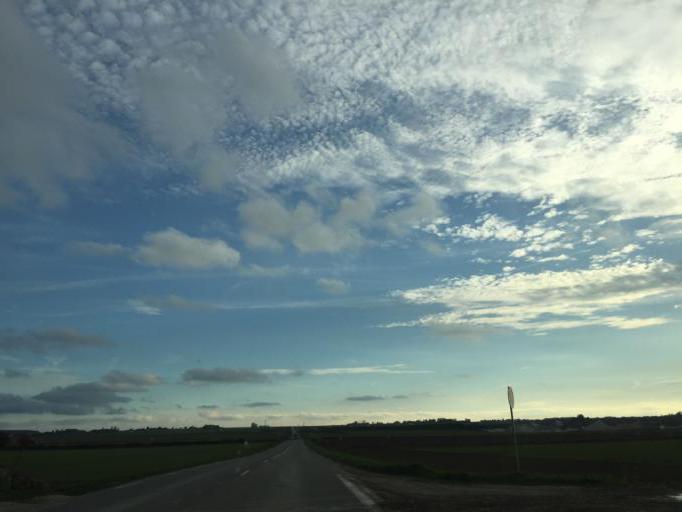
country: FR
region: Ile-de-France
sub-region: Departement de Seine-et-Marne
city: Jouy-le-Chatel
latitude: 48.6678
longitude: 3.1037
